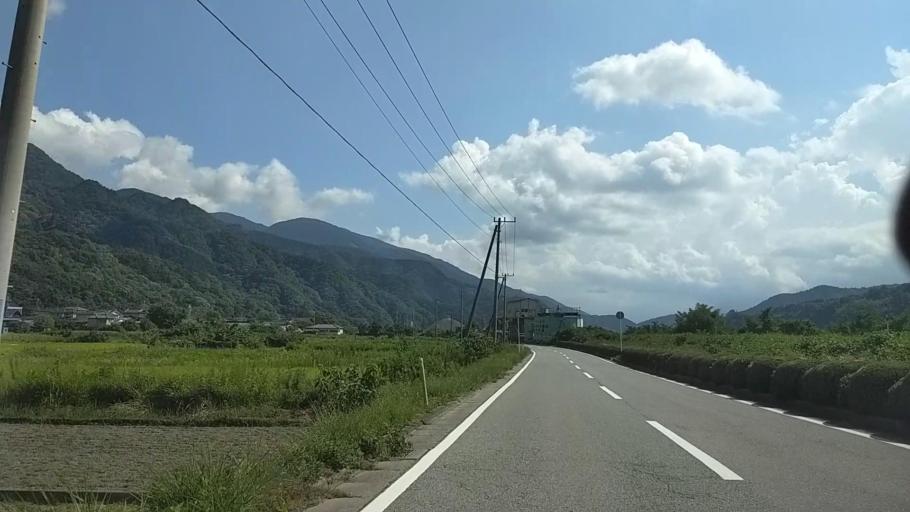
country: JP
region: Shizuoka
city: Fujinomiya
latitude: 35.3932
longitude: 138.4501
